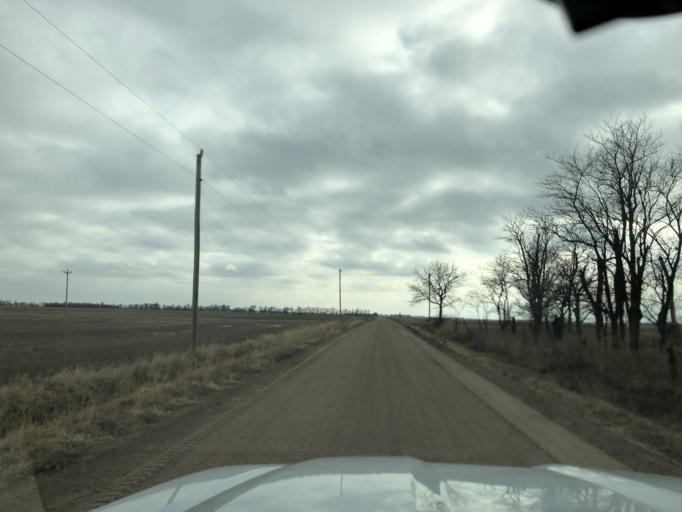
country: US
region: Kansas
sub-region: Reno County
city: Nickerson
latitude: 38.0008
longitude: -98.2157
